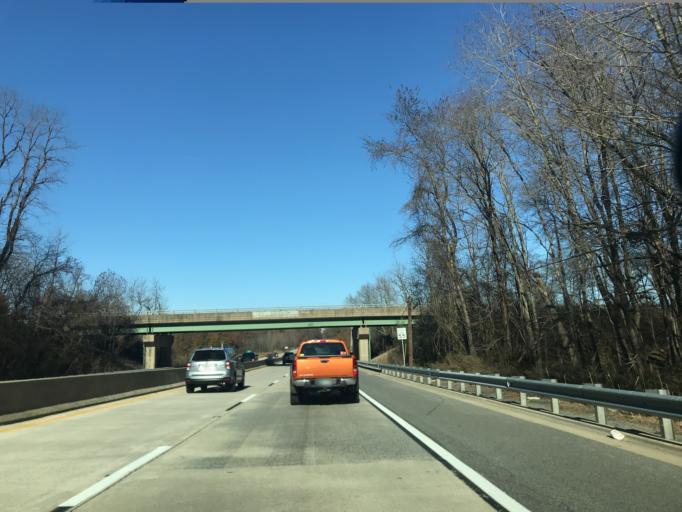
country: US
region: Delaware
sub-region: New Castle County
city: Glasgow
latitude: 39.5479
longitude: -75.7386
